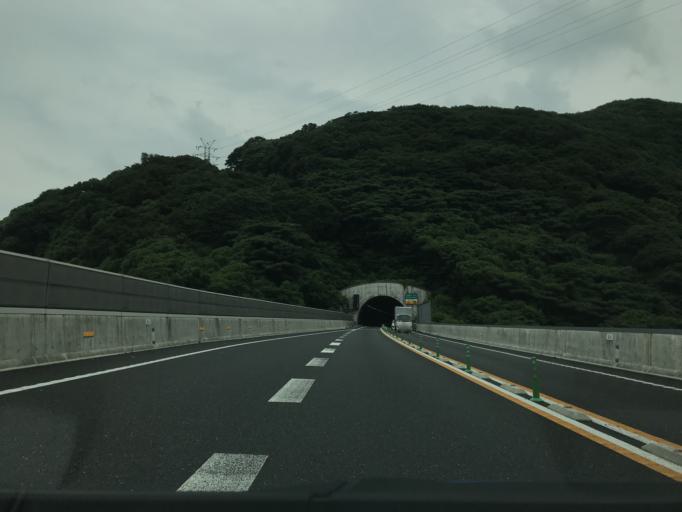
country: JP
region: Fukuoka
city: Kanda
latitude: 33.7920
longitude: 130.9689
